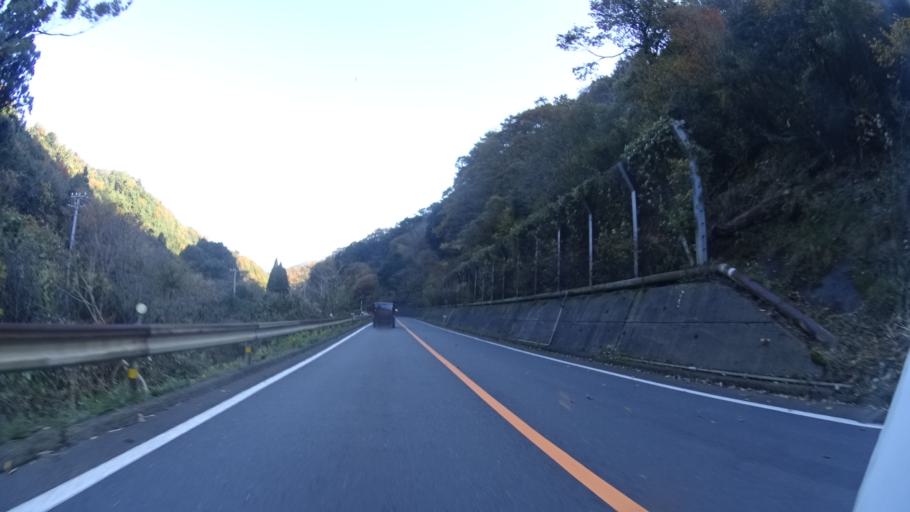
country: JP
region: Fukui
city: Tsuruga
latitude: 35.5621
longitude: 136.0977
